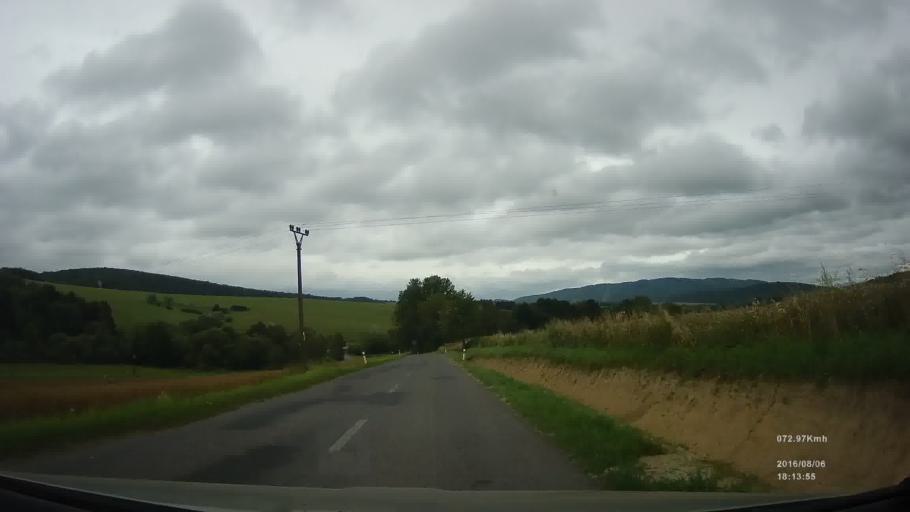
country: SK
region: Presovsky
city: Svidnik
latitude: 49.3578
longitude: 21.5924
